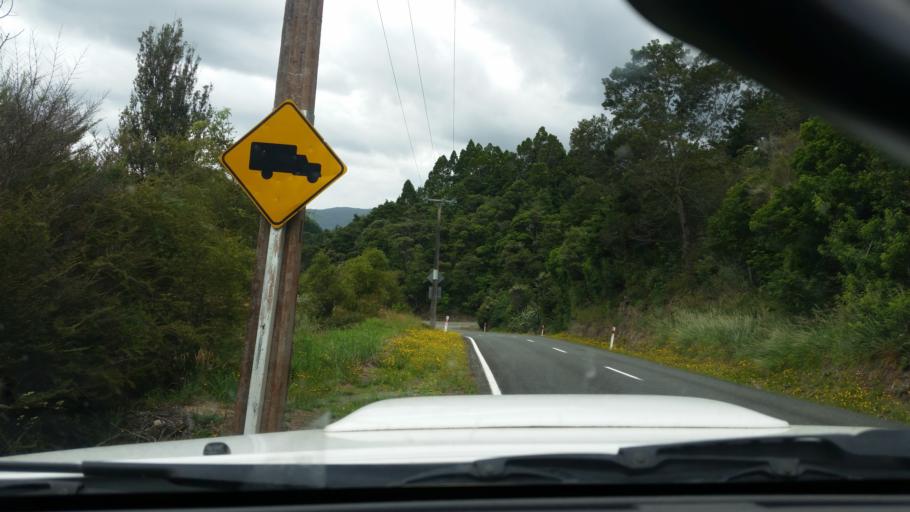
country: NZ
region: Northland
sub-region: Kaipara District
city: Dargaville
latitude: -35.8129
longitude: 173.7273
